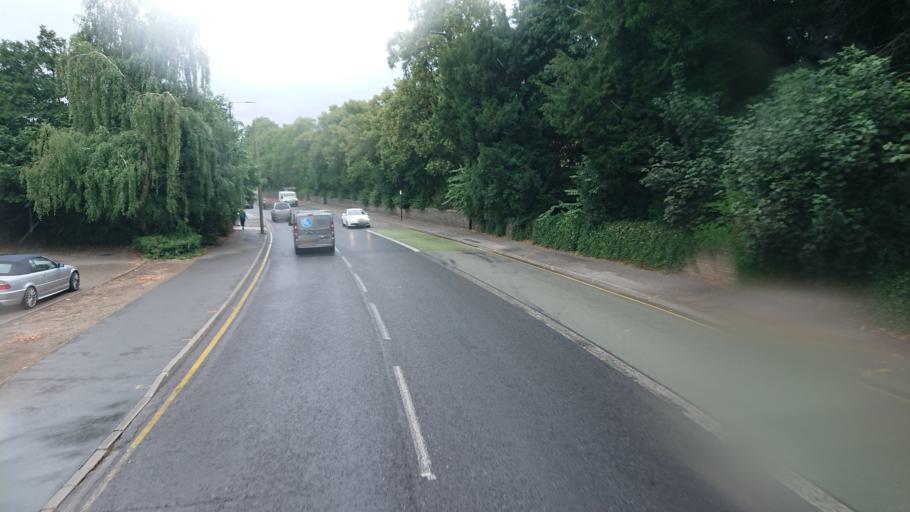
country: GB
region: England
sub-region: Sheffield
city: Sheffield
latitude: 53.3484
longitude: -1.4936
